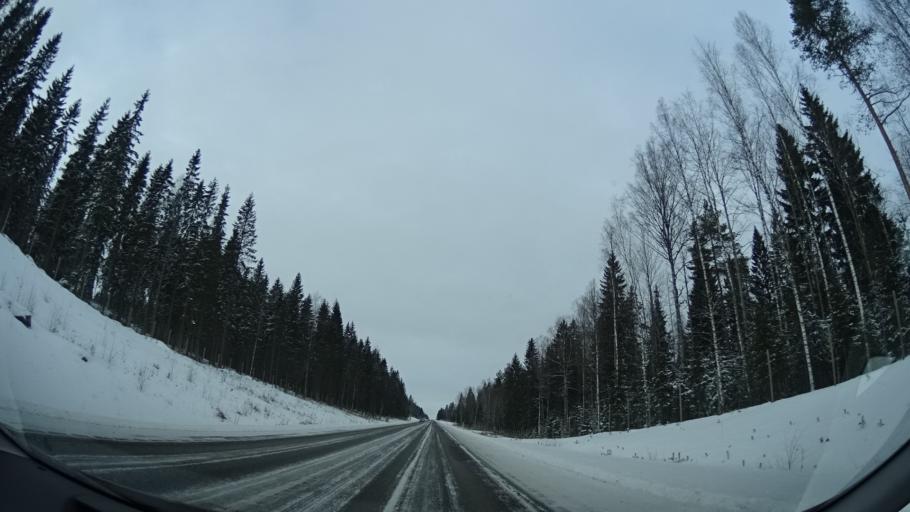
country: FI
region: Uusimaa
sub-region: Helsinki
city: Kaerkoelae
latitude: 60.6235
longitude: 23.9803
